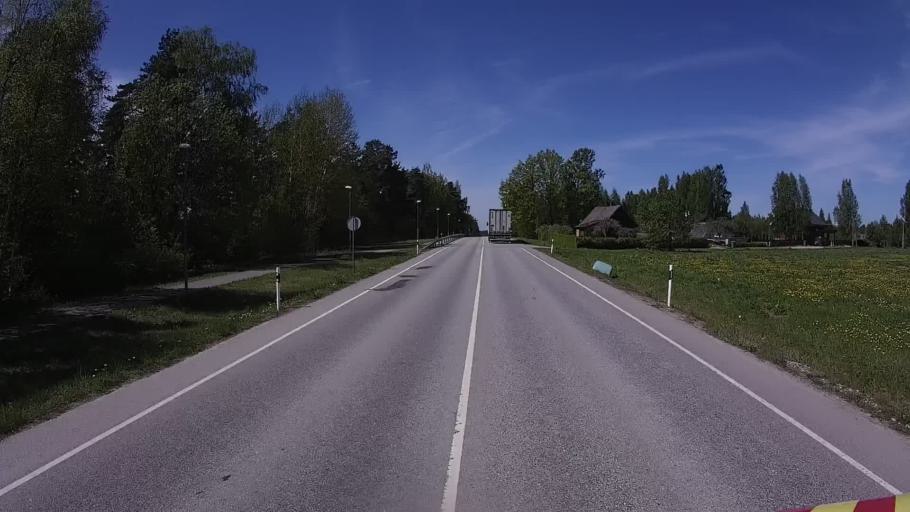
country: EE
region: Vorumaa
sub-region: Voru linn
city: Voru
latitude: 57.8116
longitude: 27.0546
